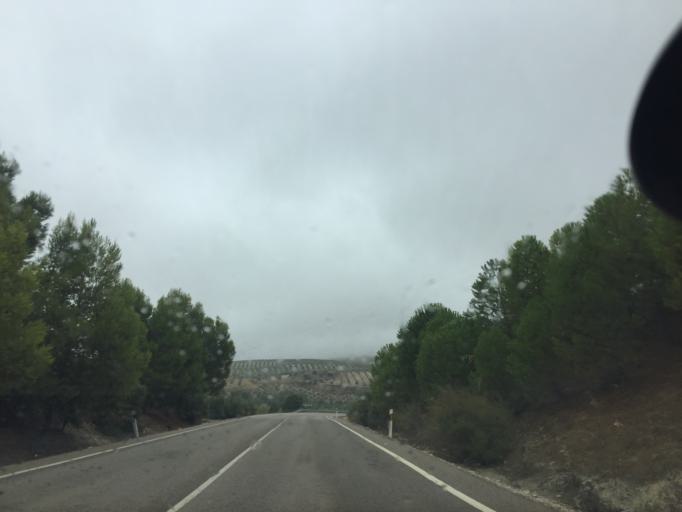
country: ES
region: Andalusia
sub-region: Provincia de Jaen
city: Torres
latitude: 37.8350
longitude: -3.5458
